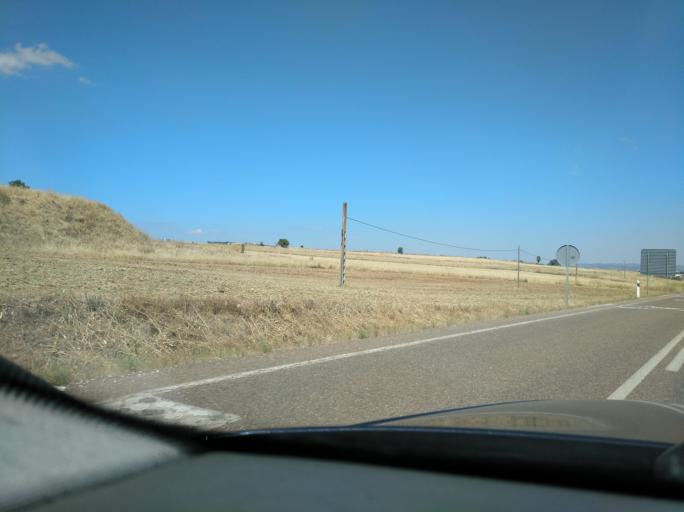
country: ES
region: Extremadura
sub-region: Provincia de Badajoz
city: Olivenza
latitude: 38.6933
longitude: -7.1010
